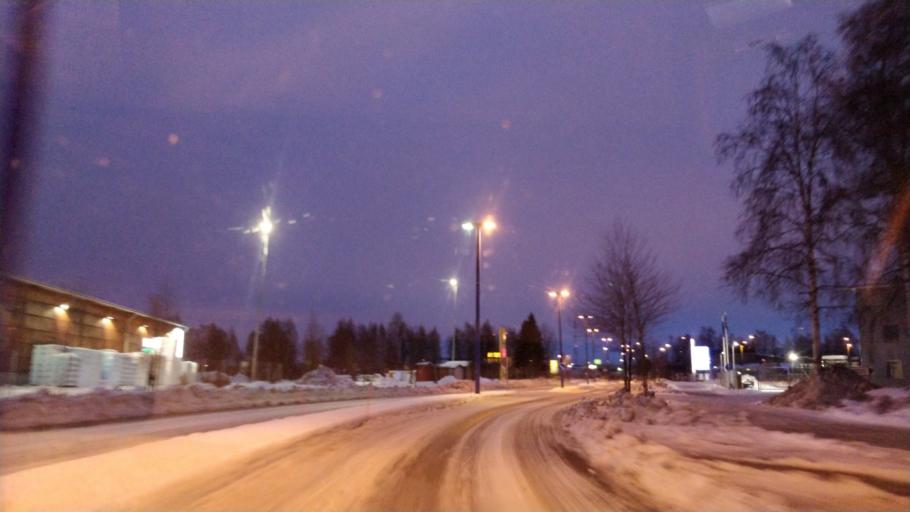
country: FI
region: Lapland
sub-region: Kemi-Tornio
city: Kemi
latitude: 65.7425
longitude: 24.5765
